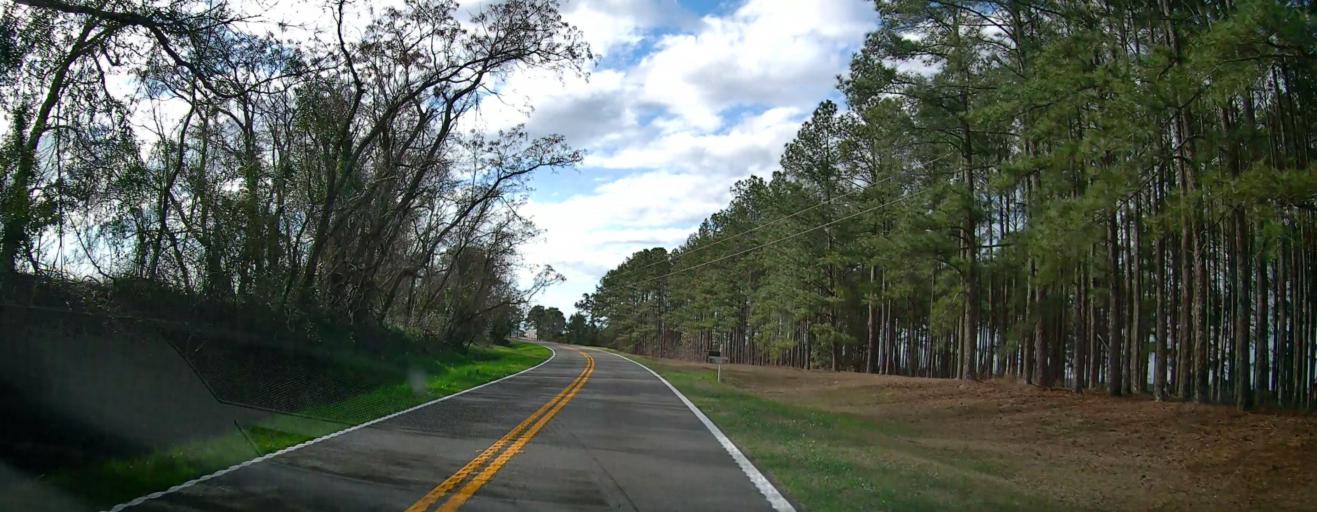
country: US
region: Georgia
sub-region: Marion County
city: Buena Vista
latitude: 32.4435
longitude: -84.5161
